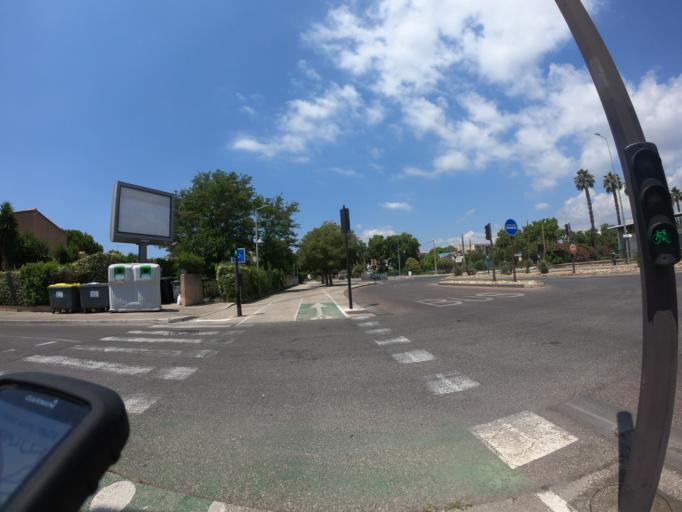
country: FR
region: Provence-Alpes-Cote d'Azur
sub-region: Departement du Var
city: La Seyne-sur-Mer
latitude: 43.1070
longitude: 5.8701
